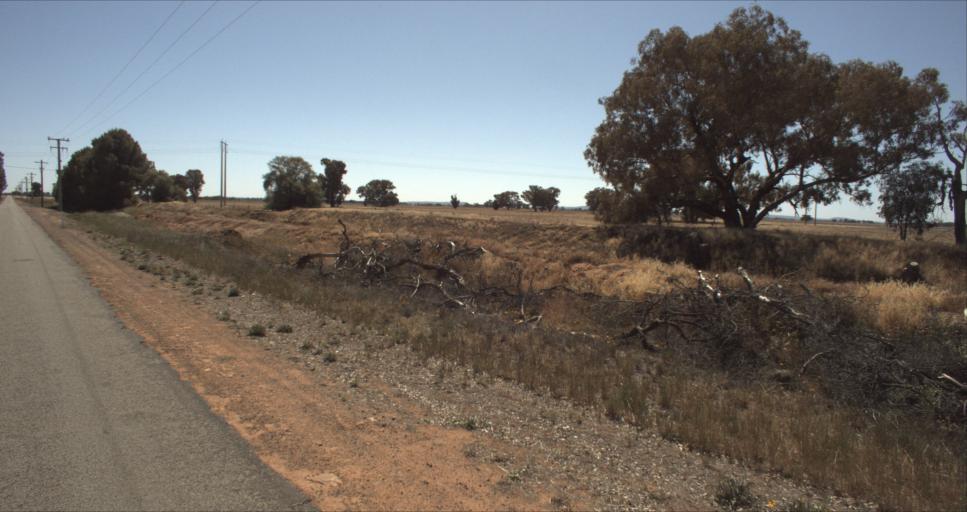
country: AU
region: New South Wales
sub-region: Leeton
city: Leeton
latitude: -34.5764
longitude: 146.3096
